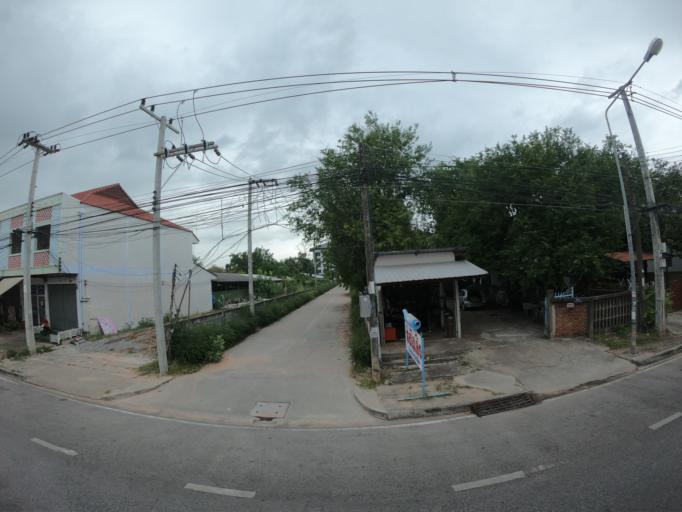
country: TH
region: Roi Et
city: Roi Et
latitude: 16.0492
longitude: 103.6392
